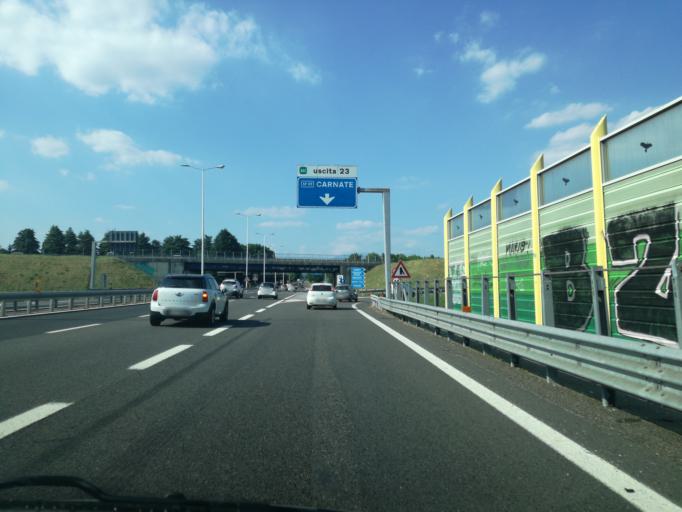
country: IT
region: Lombardy
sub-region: Provincia di Monza e Brianza
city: Usmate-Velate
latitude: 45.6408
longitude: 9.3651
